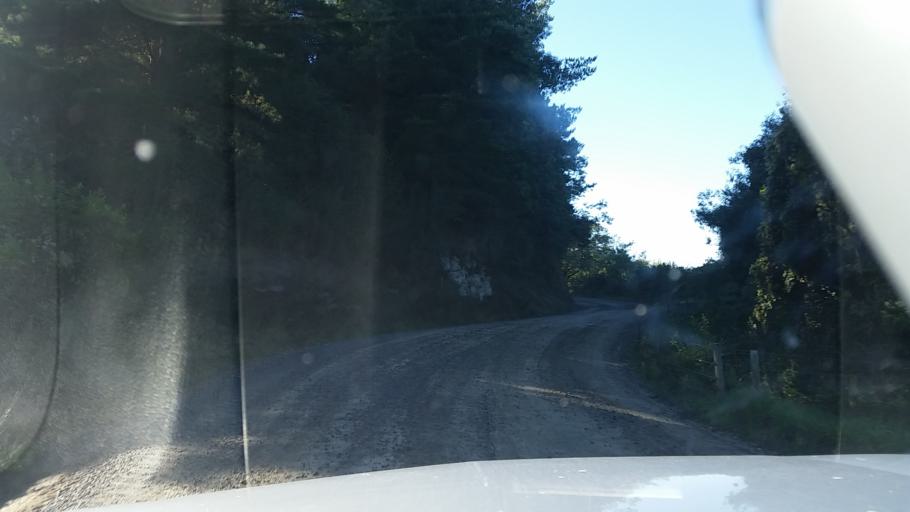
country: NZ
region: Marlborough
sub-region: Marlborough District
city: Blenheim
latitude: -41.4457
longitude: 173.8918
